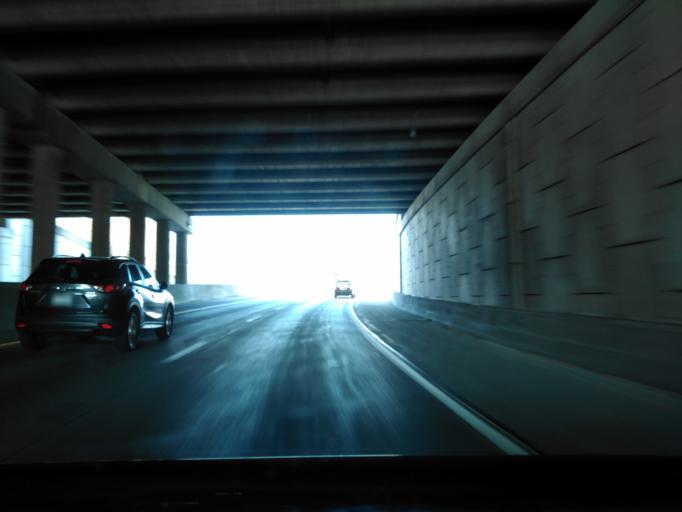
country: US
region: Missouri
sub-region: Saint Louis County
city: Valley Park
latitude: 38.5677
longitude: -90.5001
